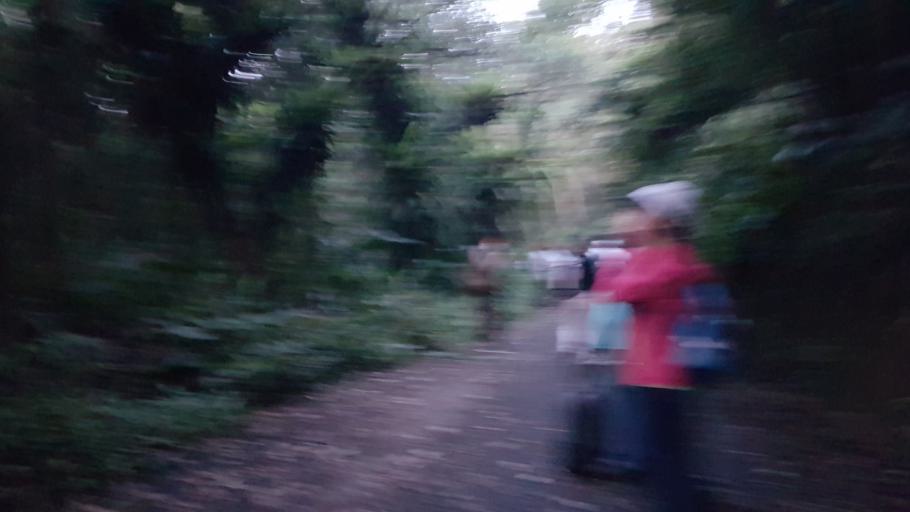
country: TW
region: Taiwan
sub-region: Yilan
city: Yilan
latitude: 24.9327
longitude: 121.7070
